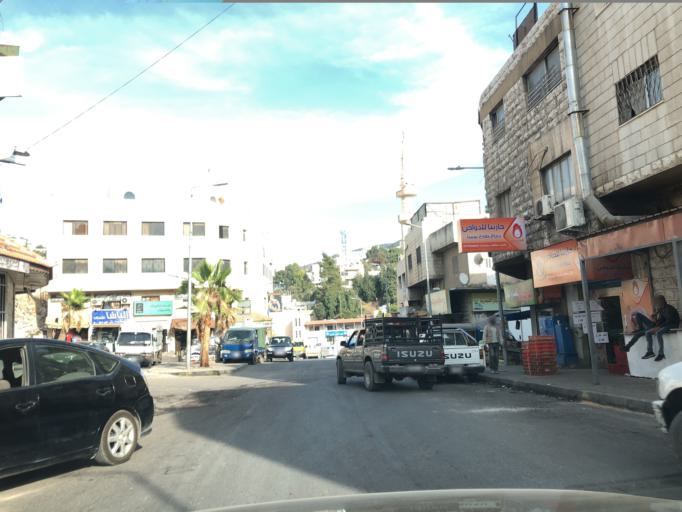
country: JO
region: Ajlun
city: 'Ajlun
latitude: 32.3325
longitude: 35.7500
